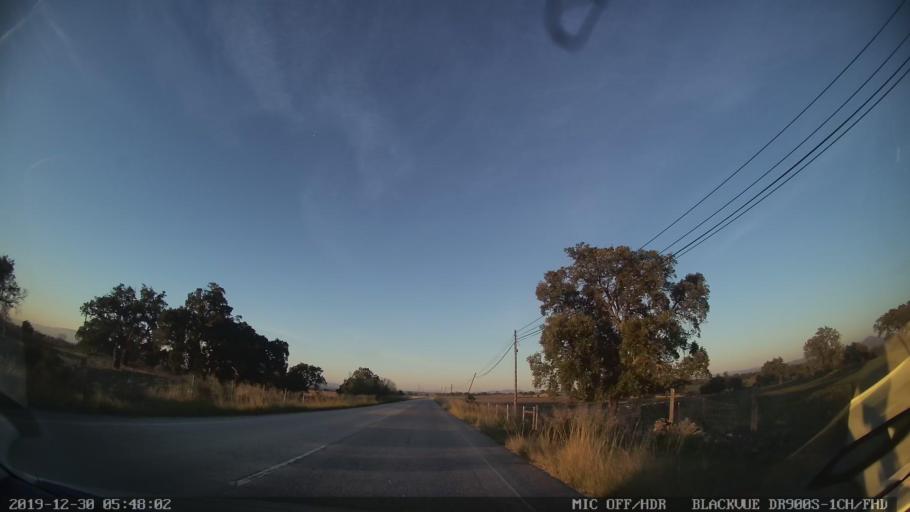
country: PT
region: Castelo Branco
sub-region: Idanha-A-Nova
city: Idanha-a-Nova
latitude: 39.9575
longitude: -7.2416
